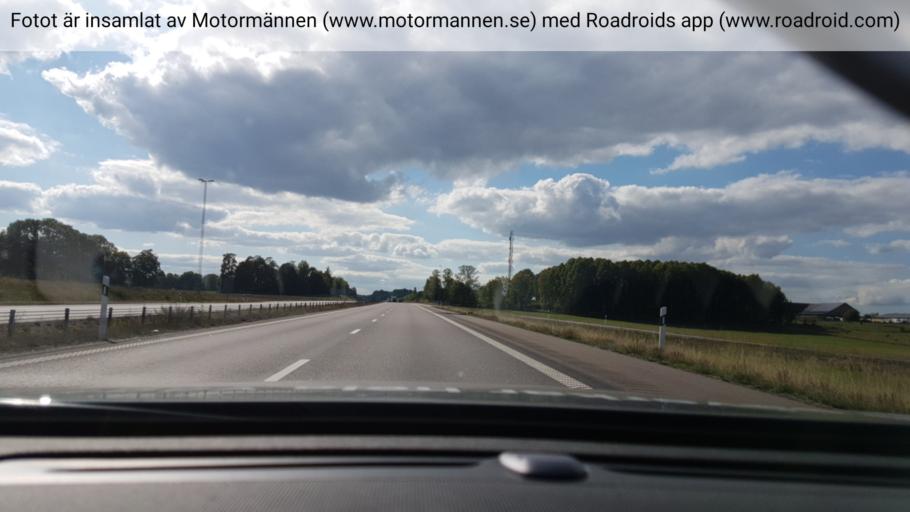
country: SE
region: OEstergoetland
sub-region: Linkopings Kommun
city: Malmslatt
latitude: 58.4342
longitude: 15.5260
